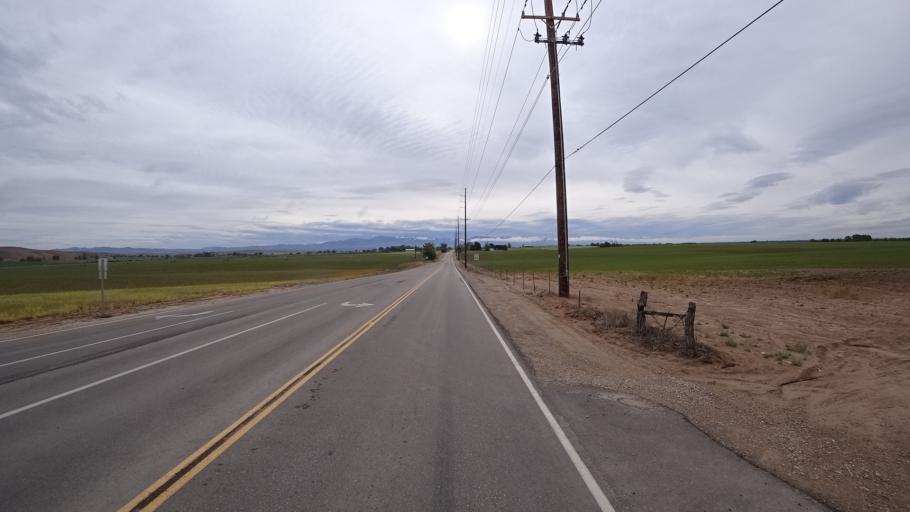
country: US
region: Idaho
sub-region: Ada County
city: Star
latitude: 43.7209
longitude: -116.4570
